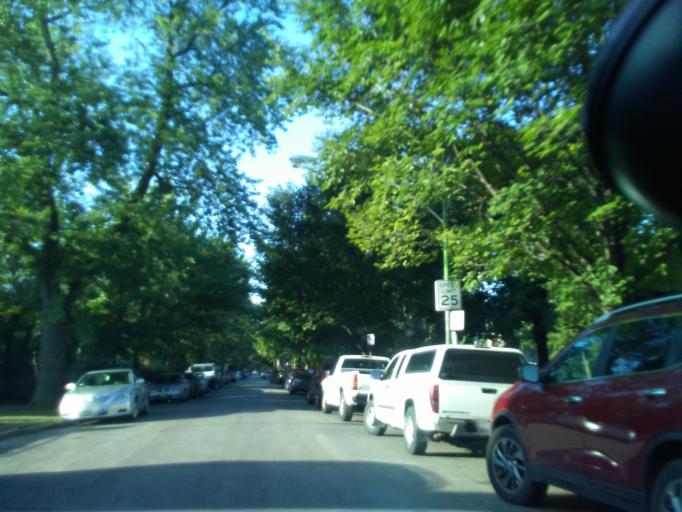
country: US
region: Illinois
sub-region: Cook County
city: Lincolnwood
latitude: 41.9311
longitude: -87.7233
